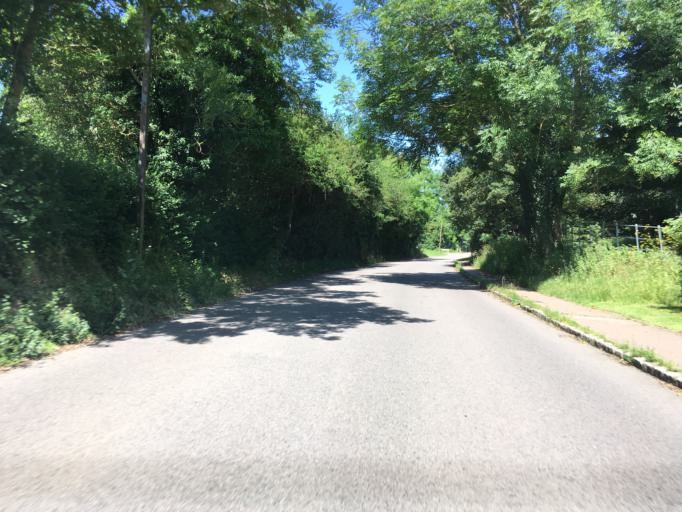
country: GB
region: England
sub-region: Milton Keynes
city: Simpson
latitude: 52.0311
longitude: -0.7243
